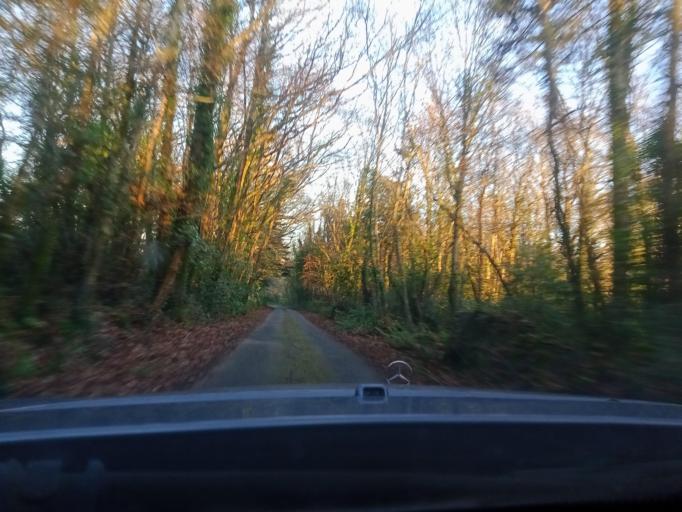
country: IE
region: Leinster
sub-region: Kilkenny
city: Graiguenamanagh
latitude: 52.4690
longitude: -6.9454
